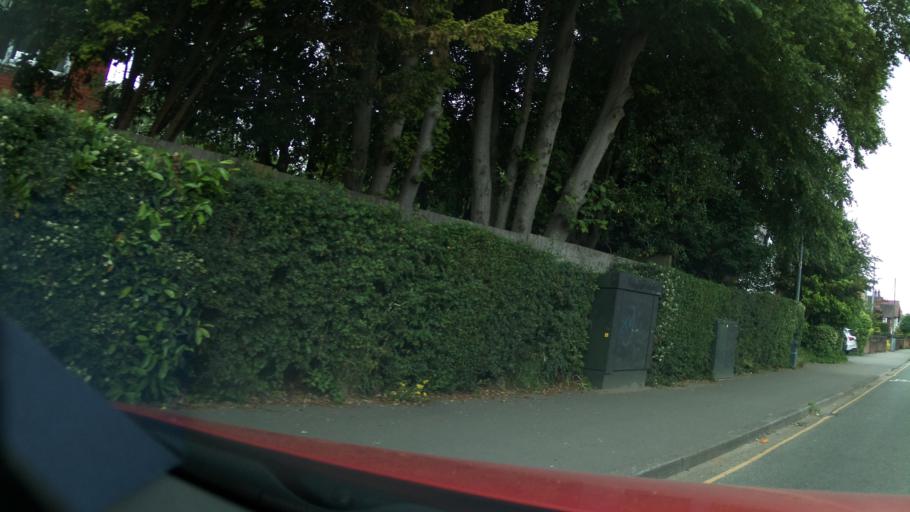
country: GB
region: England
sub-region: Leicestershire
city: Coalville
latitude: 52.7229
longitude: -1.3661
